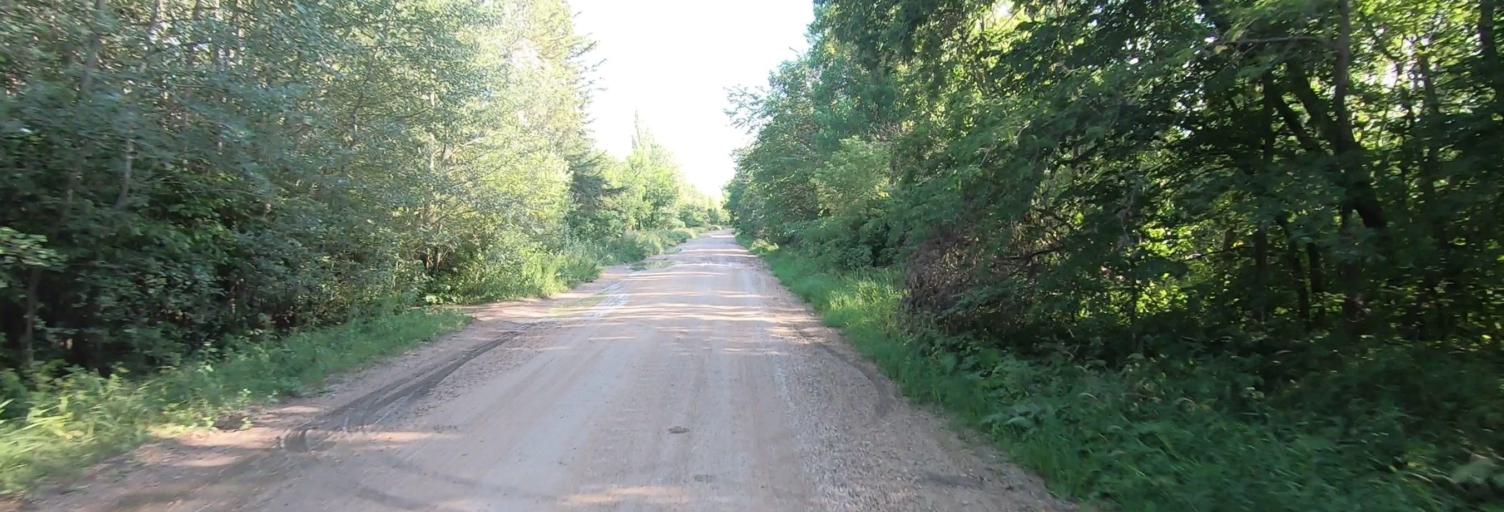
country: CA
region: Manitoba
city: Selkirk
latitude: 50.2722
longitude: -96.8499
